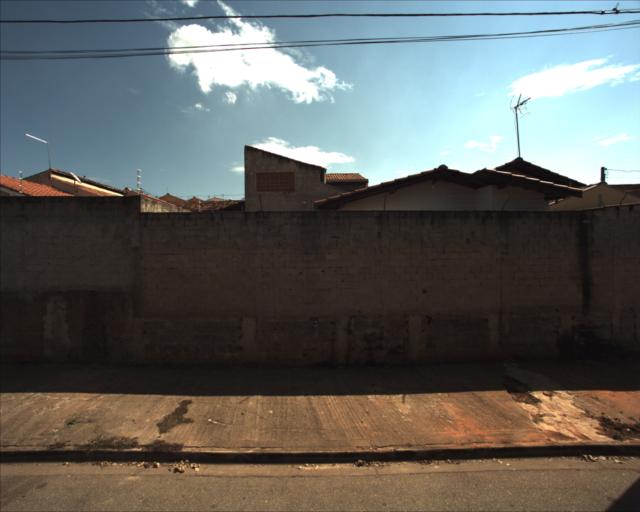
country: BR
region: Sao Paulo
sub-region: Sorocaba
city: Sorocaba
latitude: -23.4801
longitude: -47.5069
